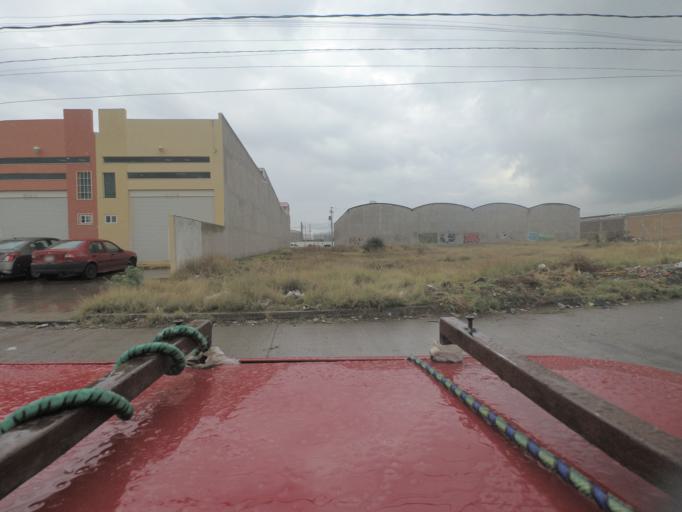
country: MX
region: Aguascalientes
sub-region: Jesus Maria
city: Arboledas Paso Blanco [Fraccionamiento]
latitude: 21.9683
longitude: -102.2931
